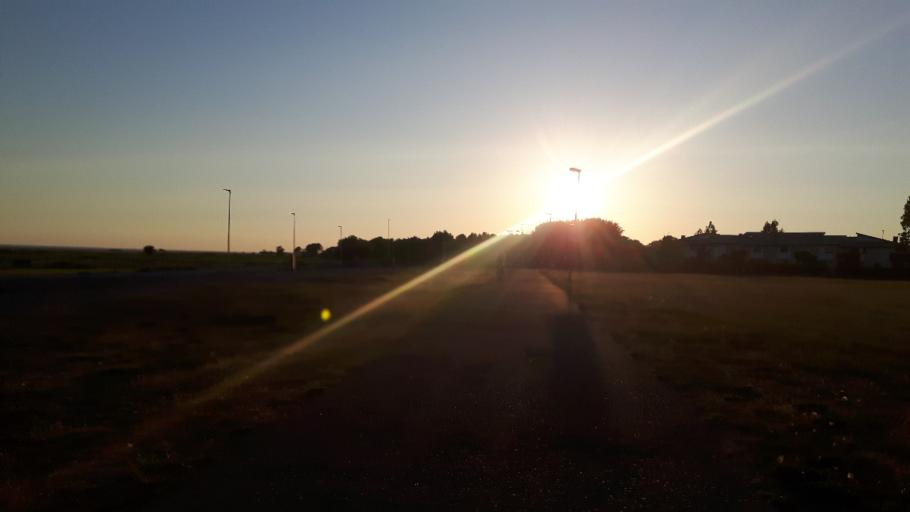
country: EE
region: Paernumaa
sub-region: Paernu linn
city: Parnu
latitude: 58.3679
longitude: 24.5359
